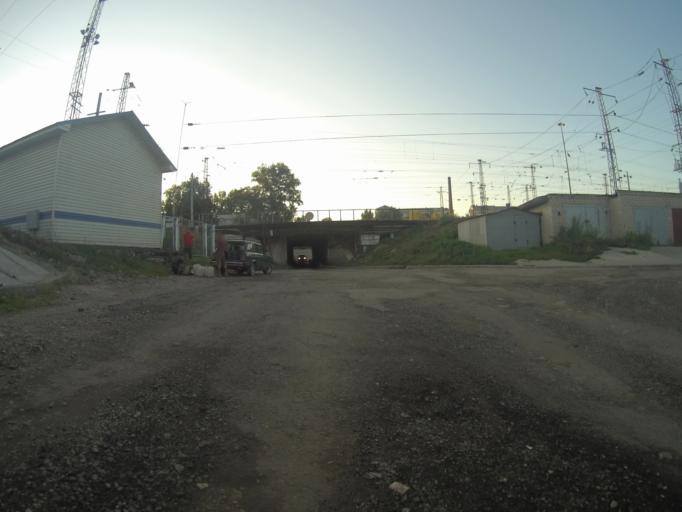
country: RU
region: Vladimir
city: Kommunar
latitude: 56.1326
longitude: 40.4279
